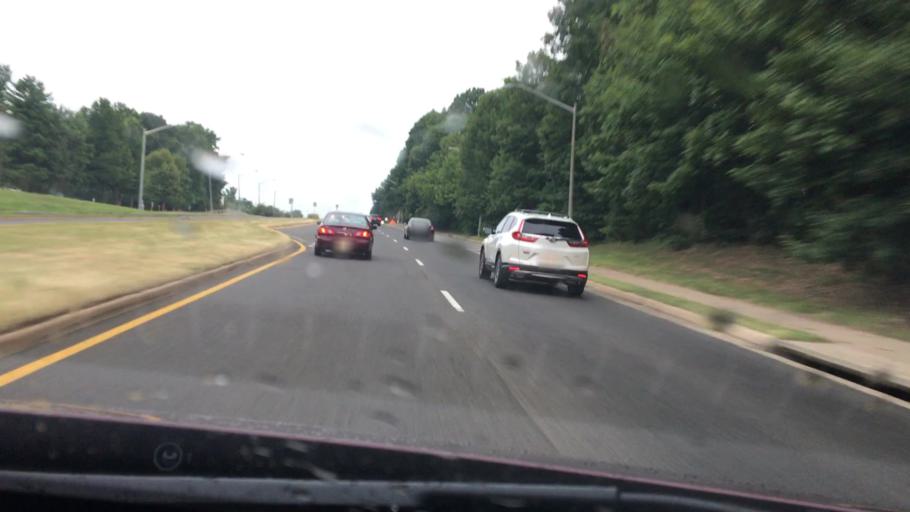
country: US
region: Virginia
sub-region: Fairfax County
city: Centreville
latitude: 38.8289
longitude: -77.4244
